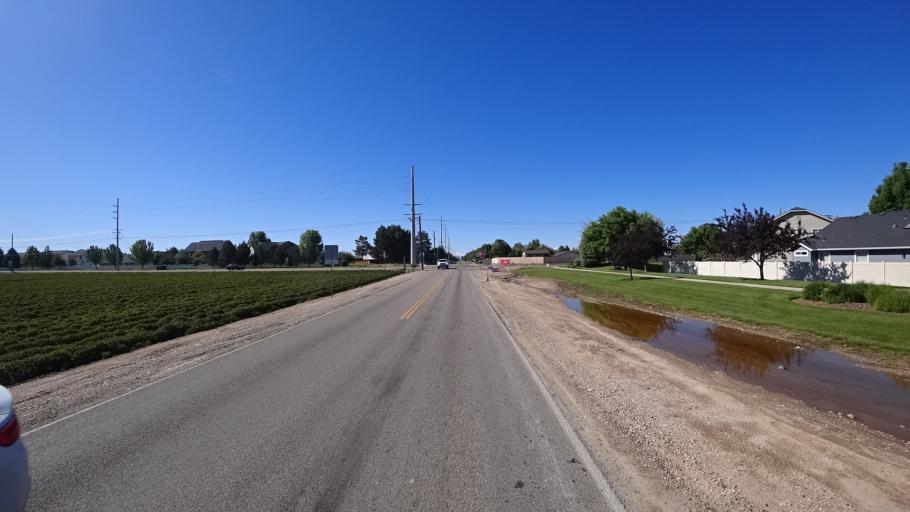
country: US
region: Idaho
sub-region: Ada County
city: Meridian
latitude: 43.6348
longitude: -116.4536
